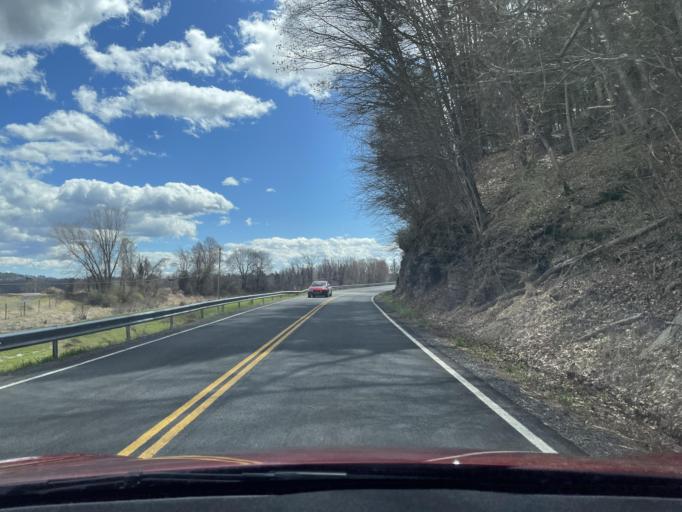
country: US
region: New York
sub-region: Ulster County
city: Hurley
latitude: 41.9379
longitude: -74.0713
